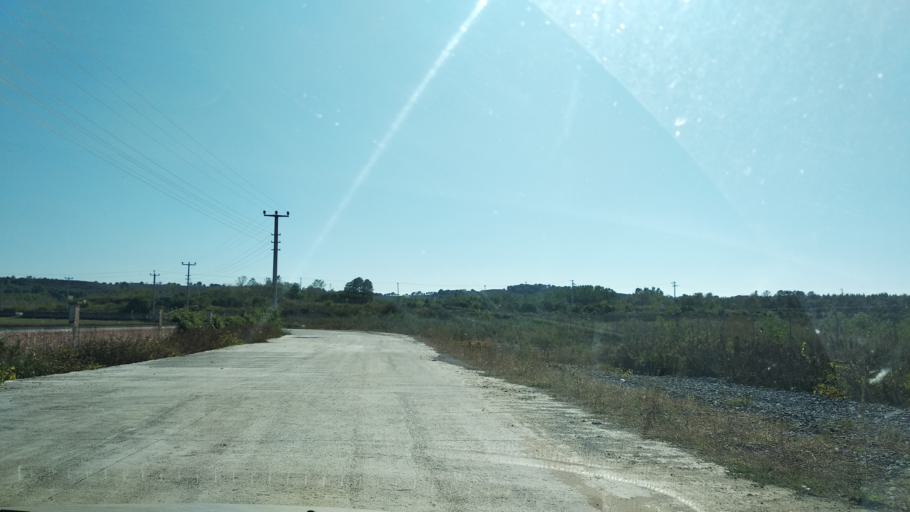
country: TR
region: Sakarya
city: Karasu
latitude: 41.1214
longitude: 30.6080
